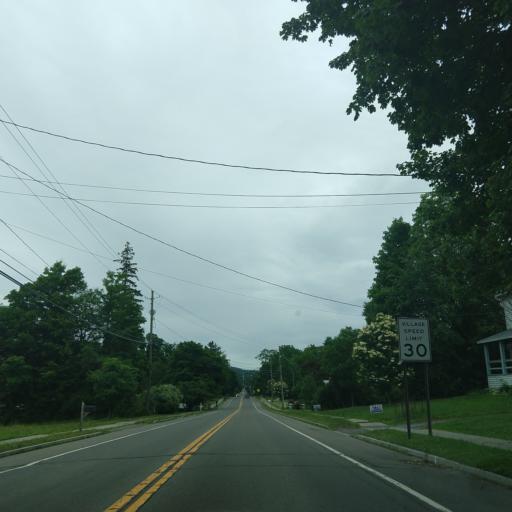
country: US
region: New York
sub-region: Tompkins County
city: Dryden
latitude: 42.4901
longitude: -76.3113
